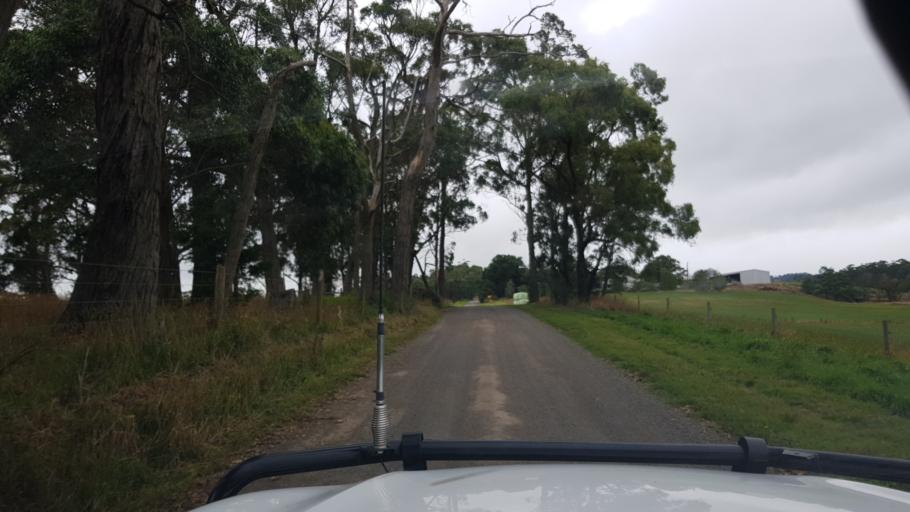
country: AU
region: Victoria
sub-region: Baw Baw
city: Warragul
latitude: -38.2382
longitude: 145.8413
